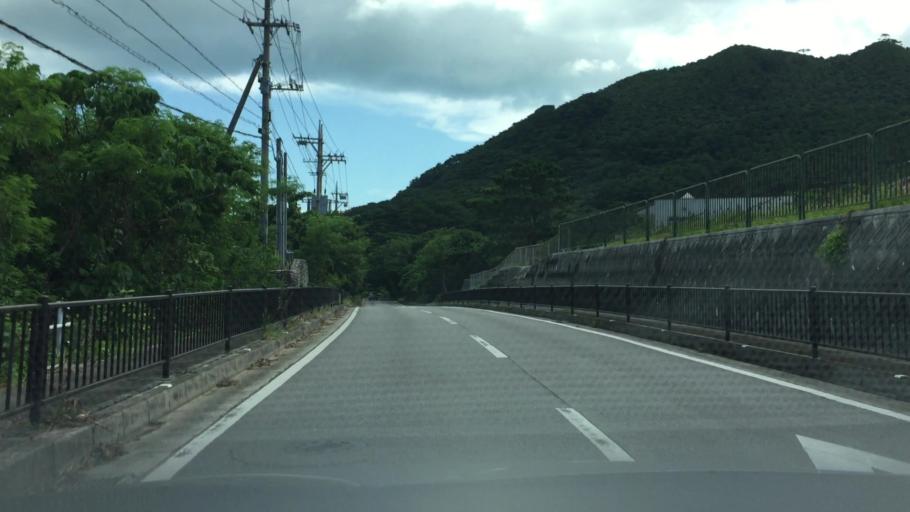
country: JP
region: Okinawa
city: Ishigaki
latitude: 24.4582
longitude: 124.1395
